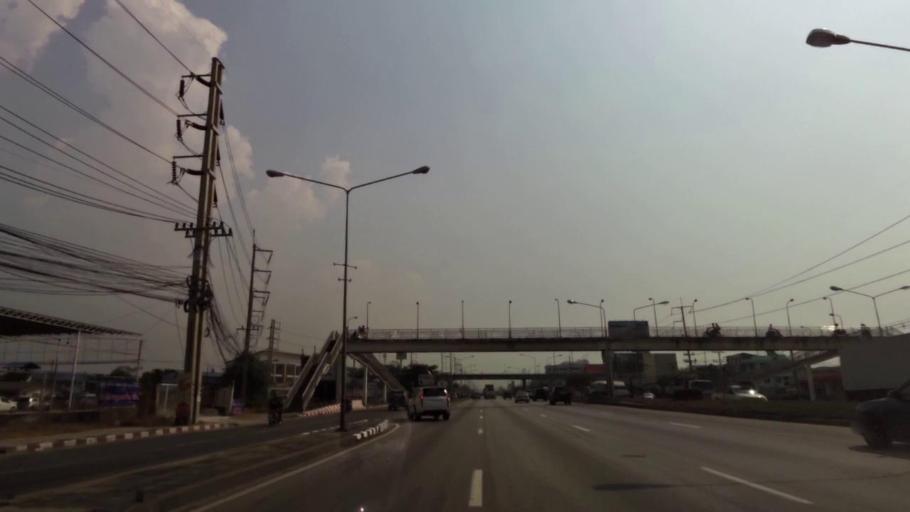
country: TH
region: Chon Buri
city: Chon Buri
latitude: 13.4018
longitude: 101.0045
